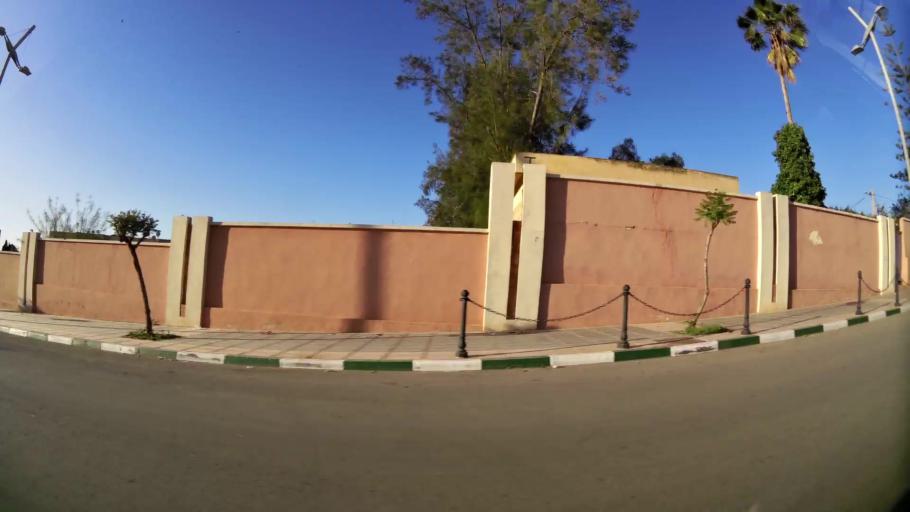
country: MA
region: Oriental
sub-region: Berkane-Taourirt
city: Berkane
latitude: 34.9252
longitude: -2.3240
